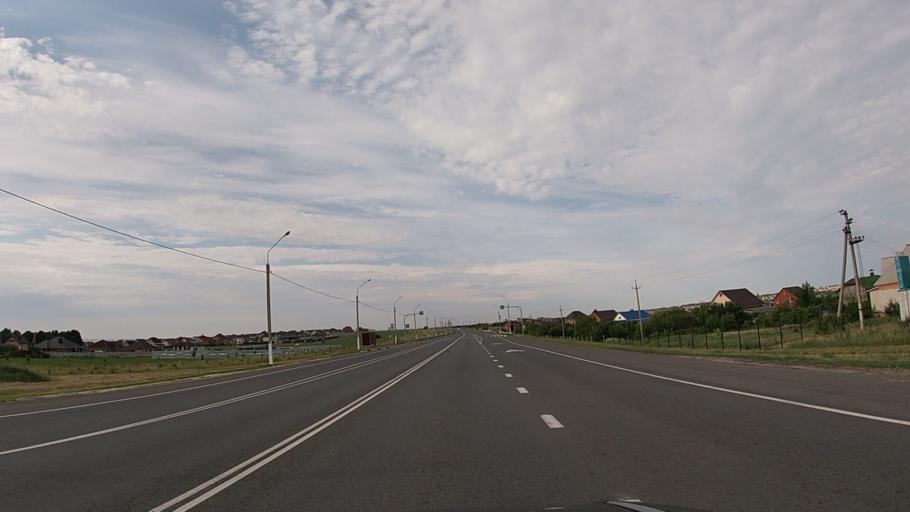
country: RU
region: Belgorod
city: Severnyy
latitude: 50.6609
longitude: 36.4684
